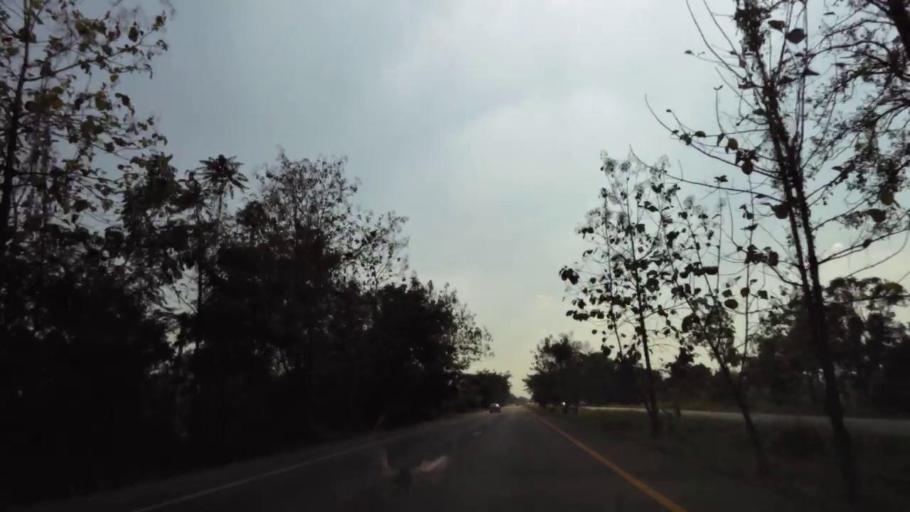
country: TH
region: Phichit
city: Bueng Na Rang
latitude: 16.2019
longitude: 100.1279
